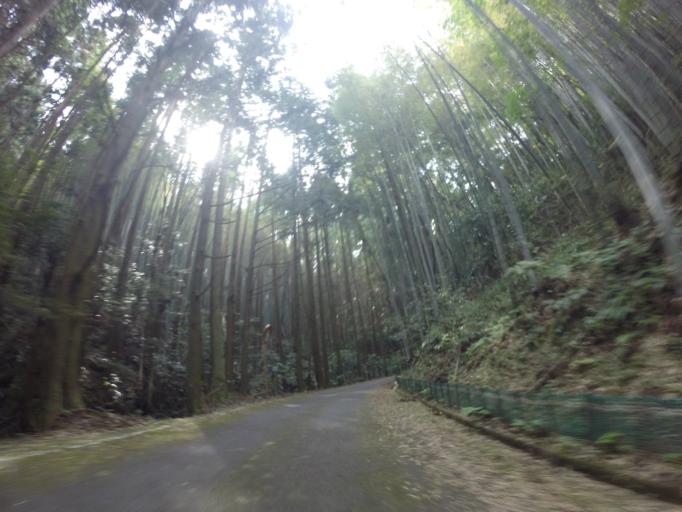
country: JP
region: Shizuoka
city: Fujieda
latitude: 34.9201
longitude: 138.2146
